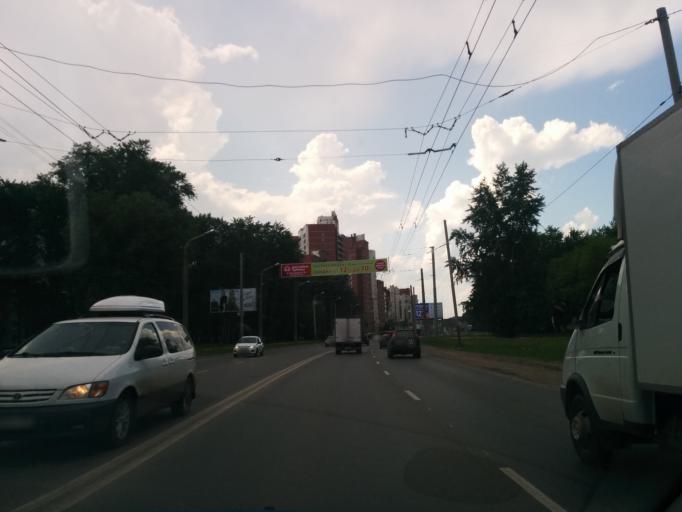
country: RU
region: Perm
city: Kondratovo
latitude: 57.9813
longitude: 56.1780
